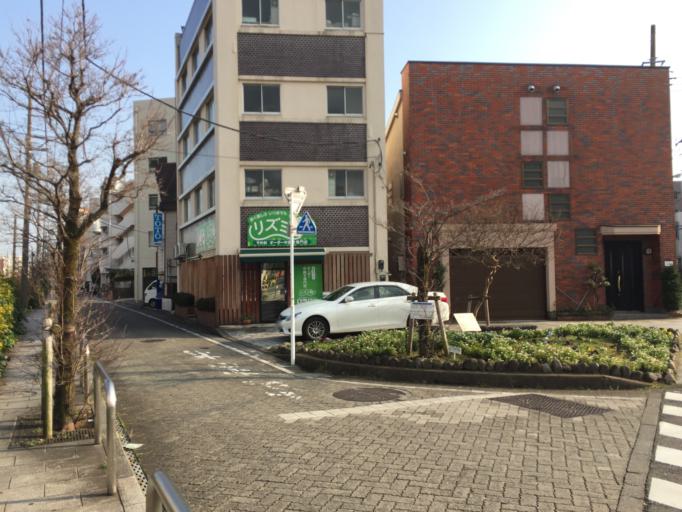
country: JP
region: Tokyo
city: Tokyo
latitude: 35.6580
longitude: 139.6428
